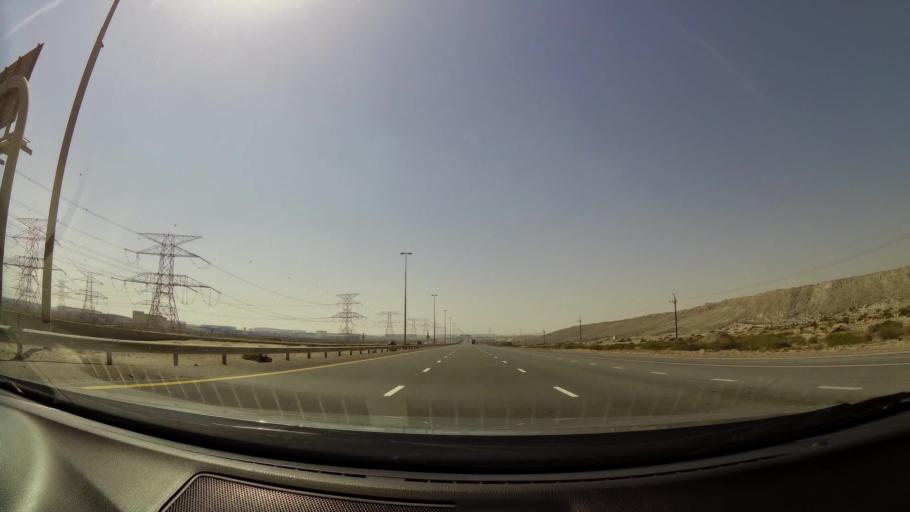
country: AE
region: Dubai
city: Dubai
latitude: 24.9337
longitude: 55.0810
